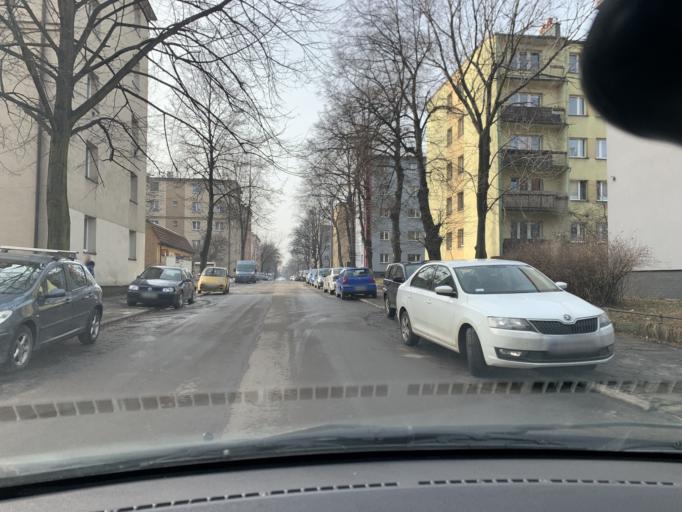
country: PL
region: Silesian Voivodeship
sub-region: Bytom
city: Bytom
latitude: 50.3553
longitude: 18.9168
